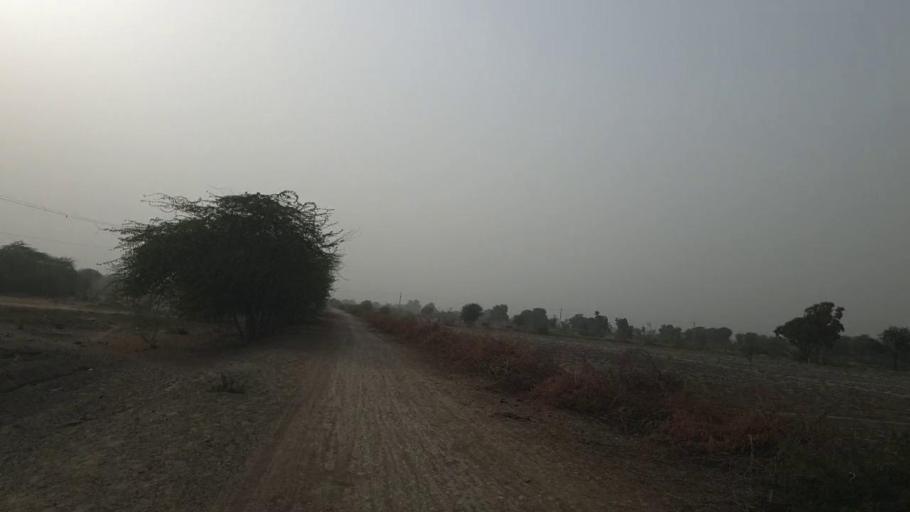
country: PK
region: Sindh
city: Kunri
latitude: 25.0669
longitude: 69.4684
